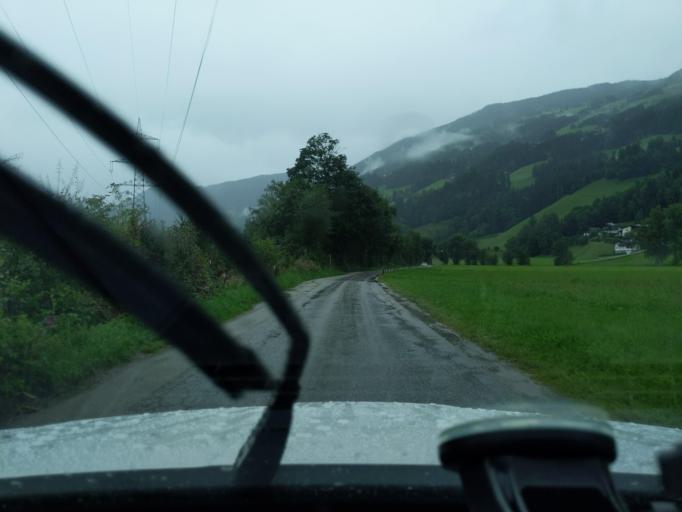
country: AT
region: Tyrol
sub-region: Politischer Bezirk Schwaz
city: Hart im Zillertal
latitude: 47.3521
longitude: 11.8646
